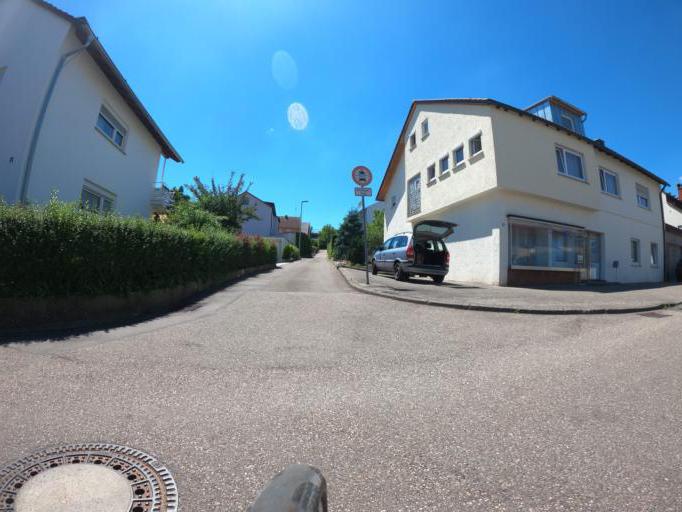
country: DE
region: Baden-Wuerttemberg
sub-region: Regierungsbezirk Stuttgart
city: Sersheim
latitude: 48.9620
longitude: 9.0541
